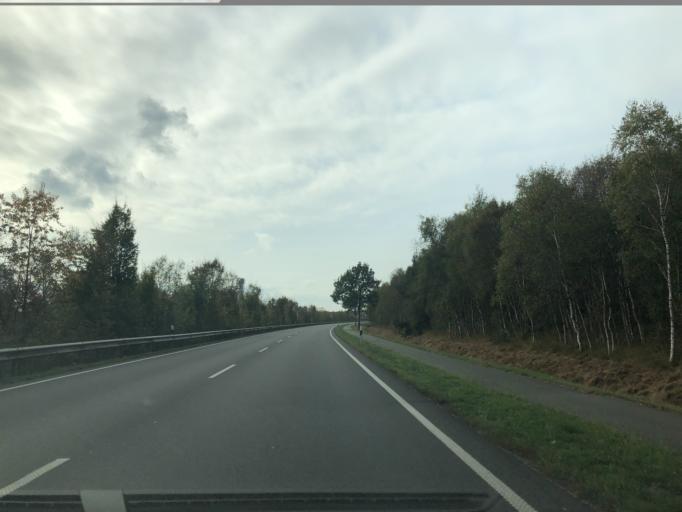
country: DE
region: Lower Saxony
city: Friesoythe
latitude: 53.0368
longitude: 7.7855
